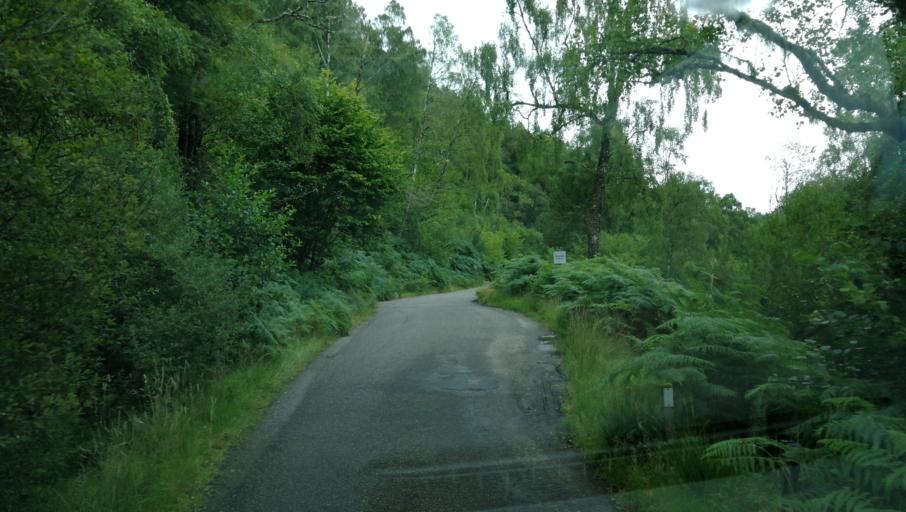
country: GB
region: Scotland
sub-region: Highland
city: Beauly
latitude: 57.3144
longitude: -4.8418
